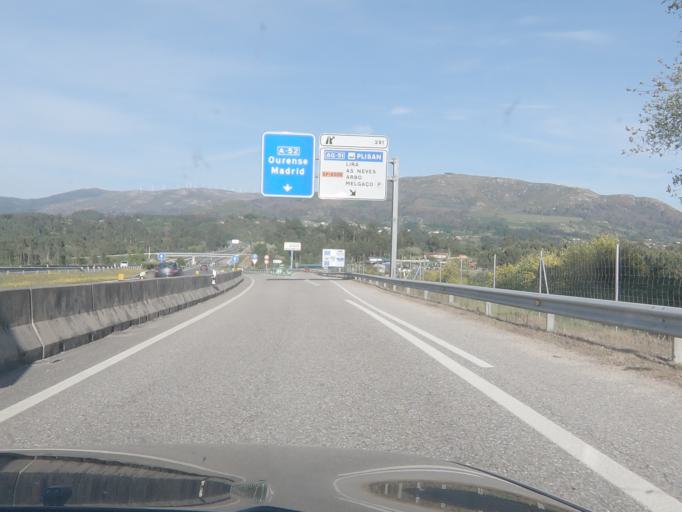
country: ES
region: Galicia
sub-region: Provincia de Pontevedra
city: Ponteareas
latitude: 42.1424
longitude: -8.4679
